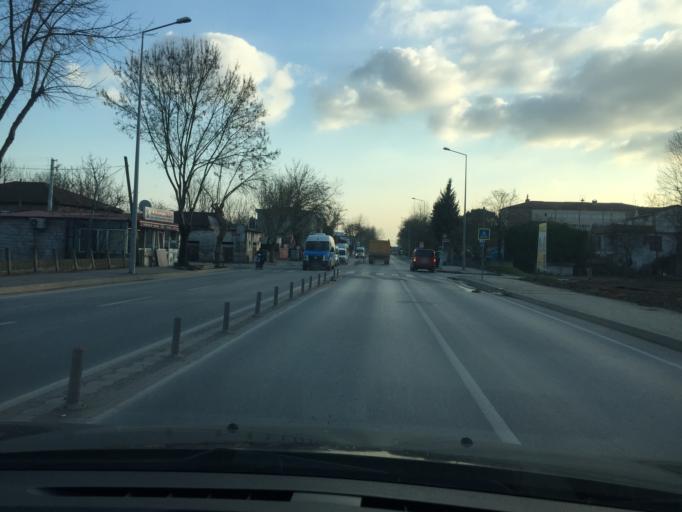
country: TR
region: Sakarya
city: Adapazari
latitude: 40.7972
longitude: 30.4067
